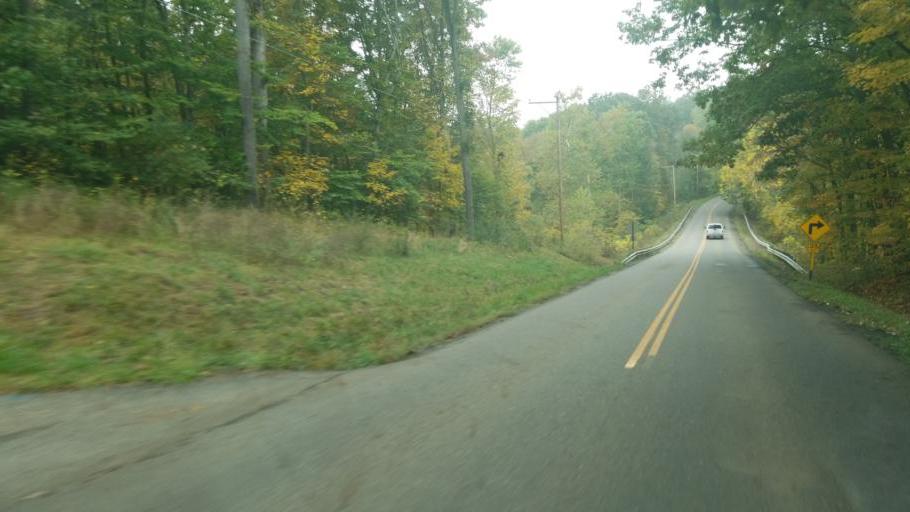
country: US
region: Ohio
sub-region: Tuscarawas County
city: Strasburg
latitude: 40.6389
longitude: -81.4001
